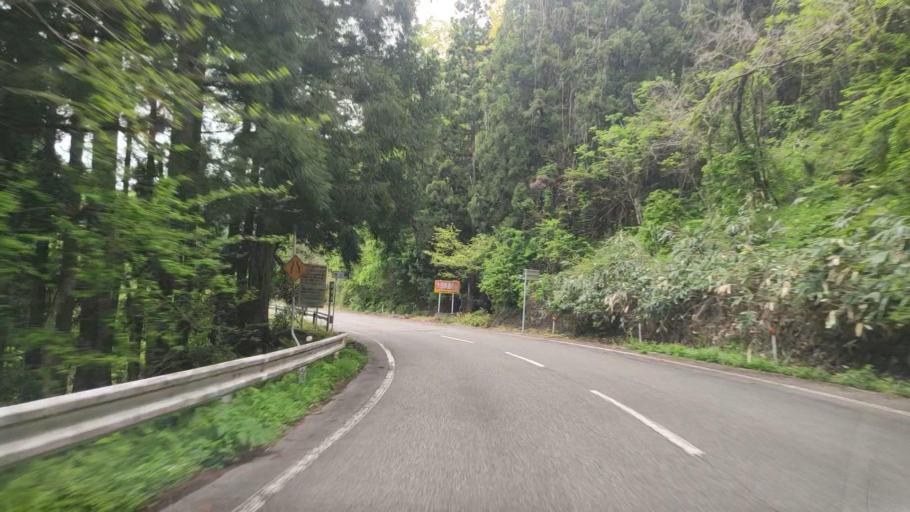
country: JP
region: Niigata
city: Gosen
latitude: 37.7103
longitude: 139.0951
